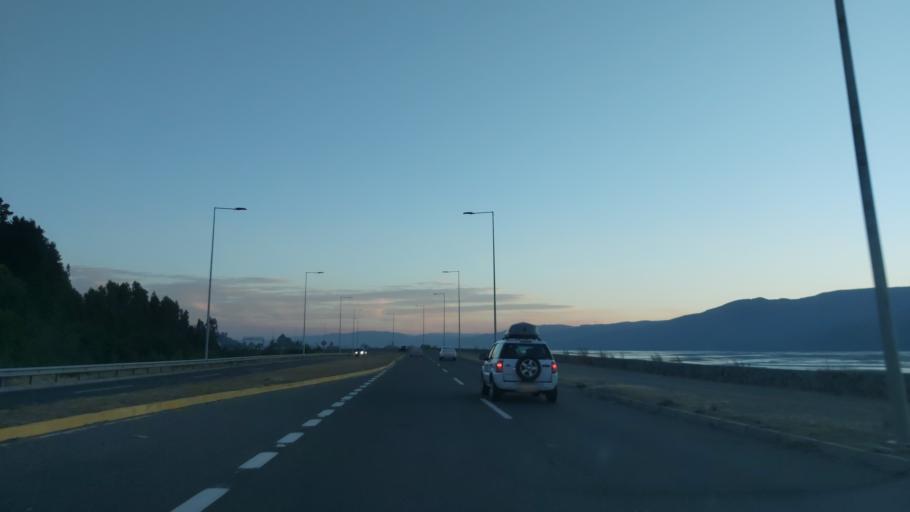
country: CL
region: Biobio
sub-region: Provincia de Concepcion
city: Concepcion
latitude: -36.8692
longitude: -73.0440
